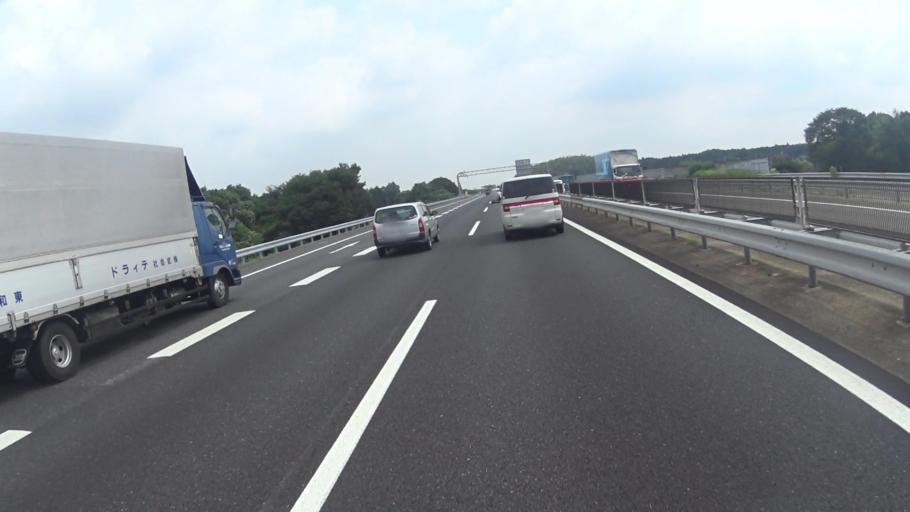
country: JP
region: Mie
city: Kameyama
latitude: 34.9099
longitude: 136.4745
